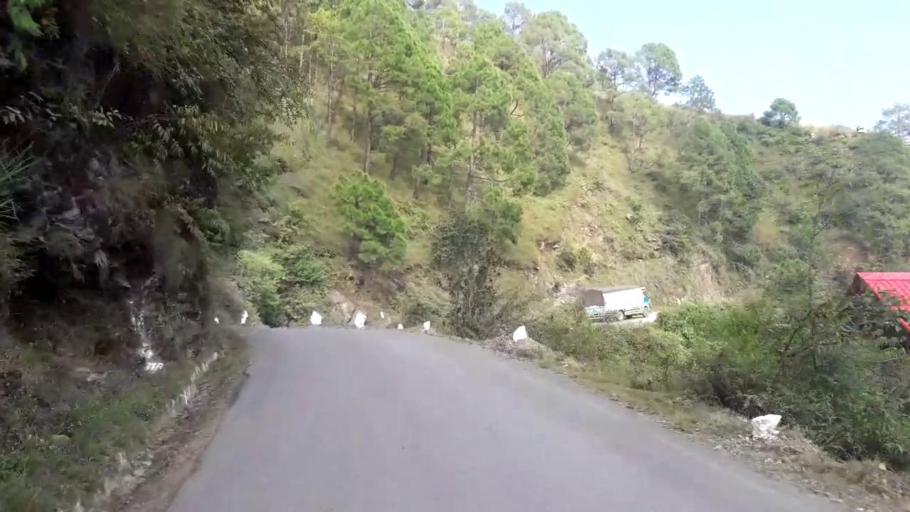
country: IN
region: Himachal Pradesh
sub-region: Shimla
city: Jutogh
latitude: 31.0494
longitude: 77.1415
